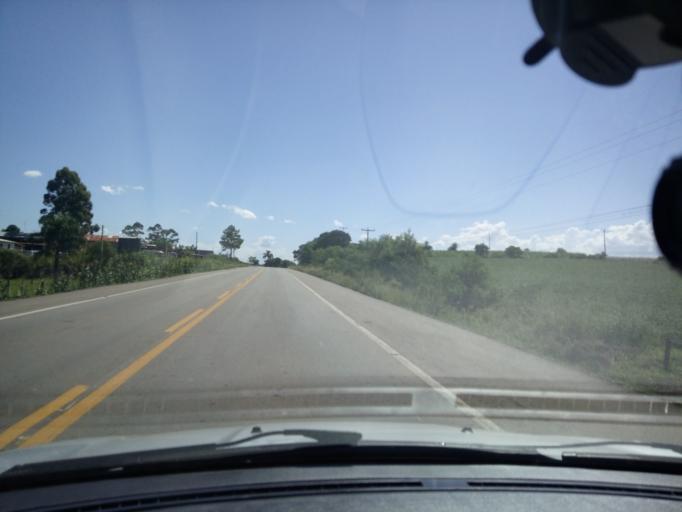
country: BR
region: Rio Grande do Sul
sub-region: Santa Maria
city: Santa Maria
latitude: -29.7328
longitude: -53.5213
